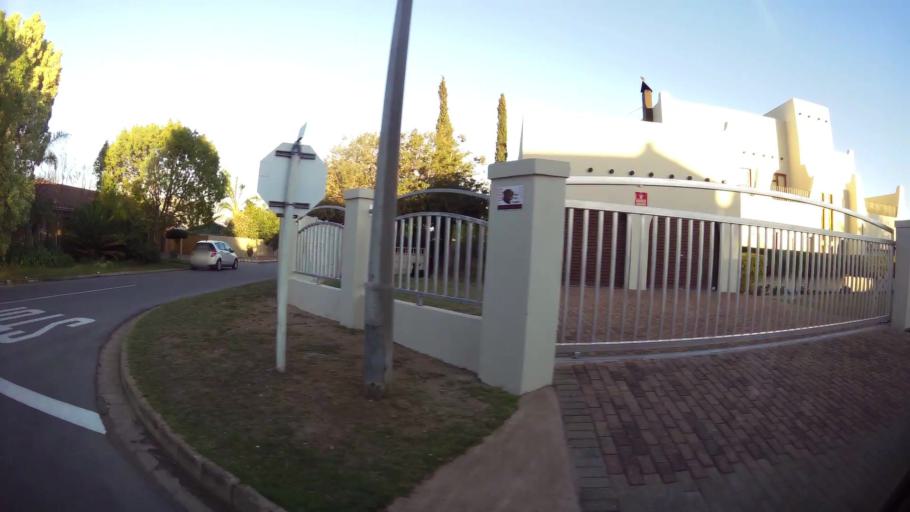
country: ZA
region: Western Cape
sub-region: Eden District Municipality
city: Riversdale
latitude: -34.0863
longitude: 21.2417
